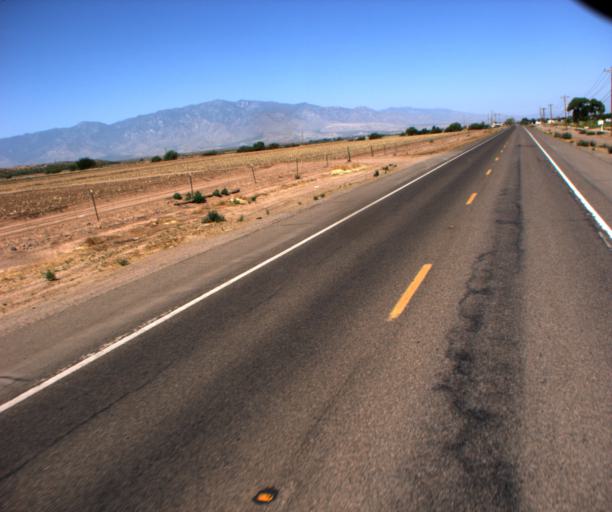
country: US
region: Arizona
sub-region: Graham County
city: Safford
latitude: 32.8128
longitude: -109.6096
